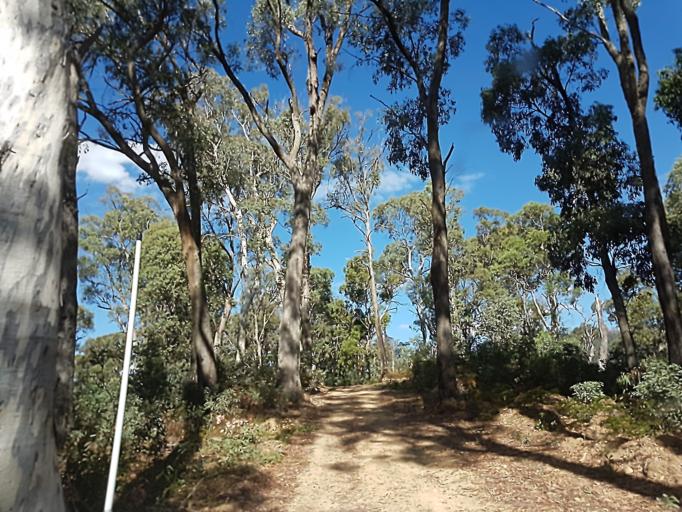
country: AU
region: Victoria
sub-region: Alpine
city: Mount Beauty
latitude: -36.9328
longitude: 147.0119
